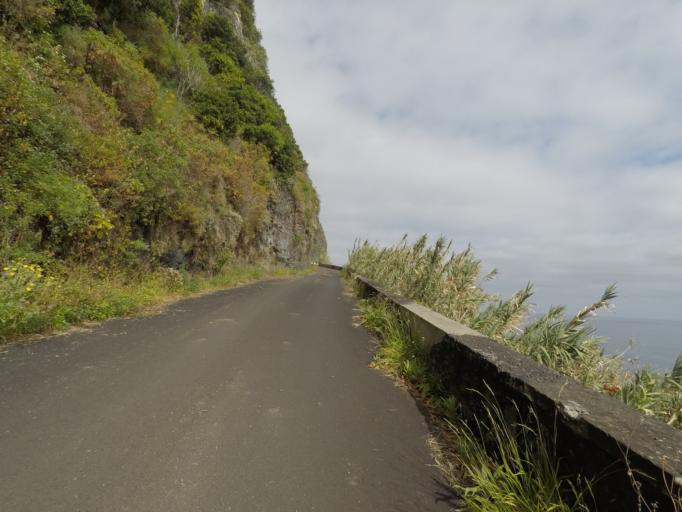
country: PT
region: Madeira
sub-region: Sao Vicente
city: Sao Vicente
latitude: 32.8109
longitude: -17.0615
